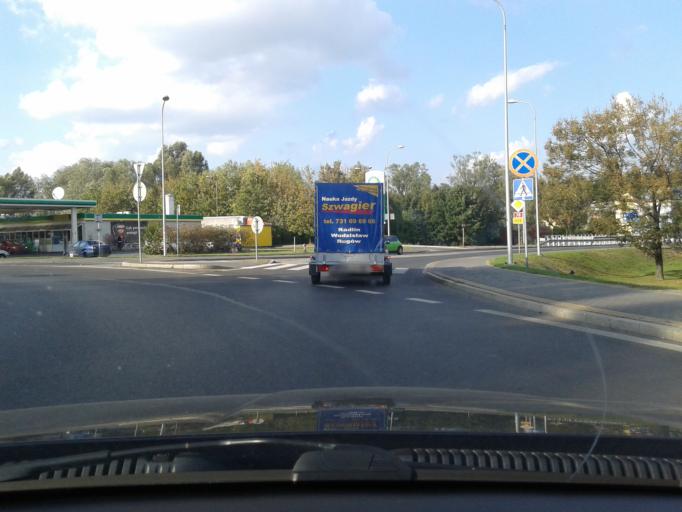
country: PL
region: Silesian Voivodeship
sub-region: Rybnik
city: Rybnik
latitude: 50.1000
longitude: 18.5350
